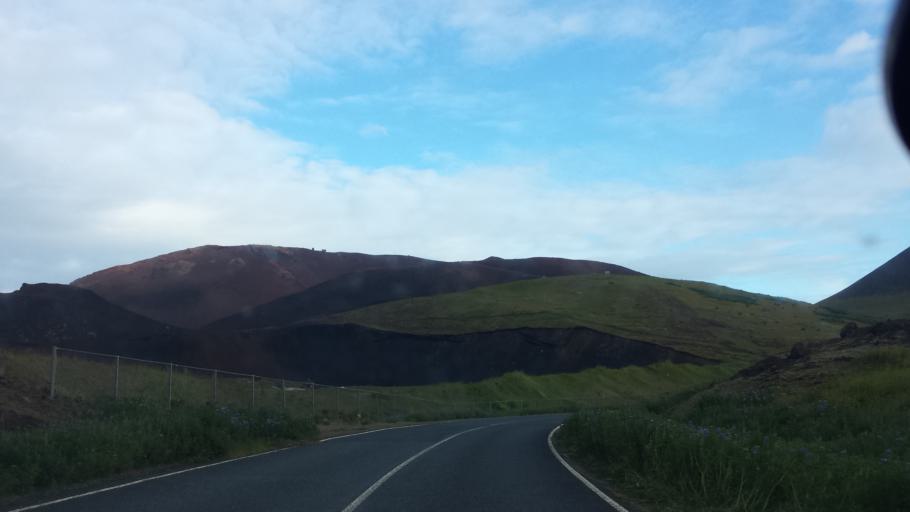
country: IS
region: South
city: Vestmannaeyjar
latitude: 63.4386
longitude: -20.2565
